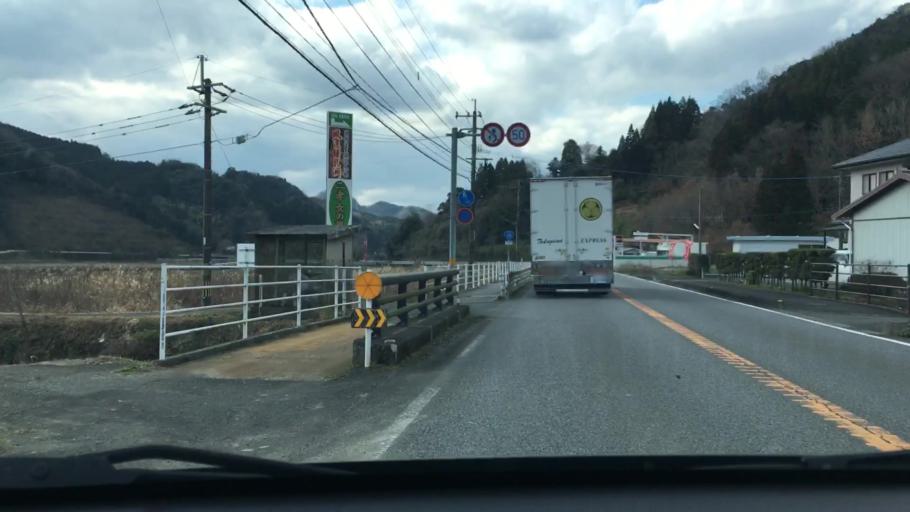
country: JP
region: Oita
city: Usuki
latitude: 33.0053
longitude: 131.7328
